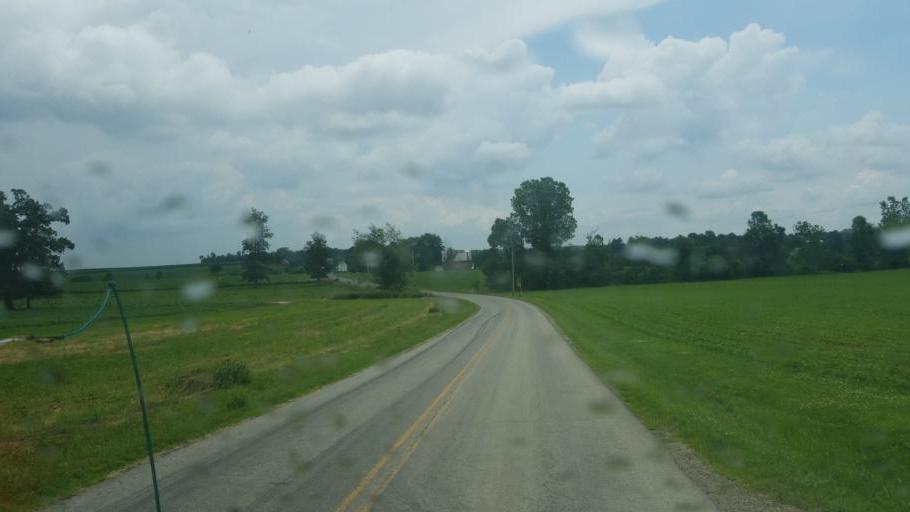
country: US
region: Ohio
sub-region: Wayne County
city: West Salem
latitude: 40.8576
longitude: -82.1115
